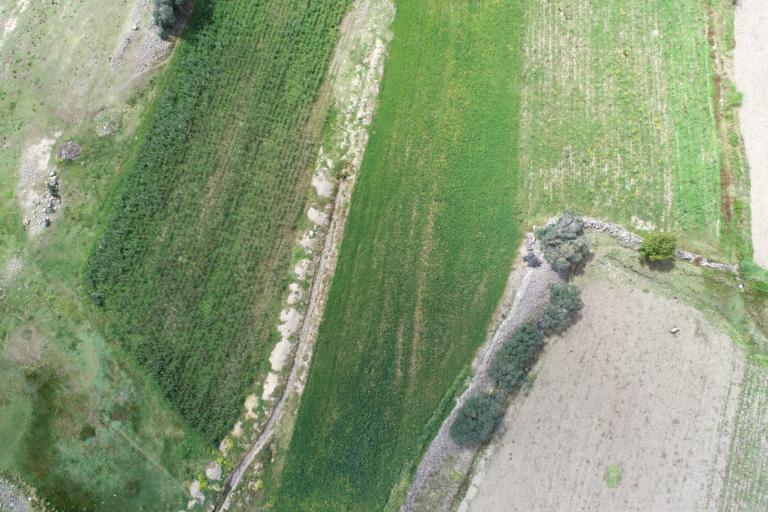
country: BO
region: La Paz
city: Achacachi
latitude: -16.0228
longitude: -68.6174
